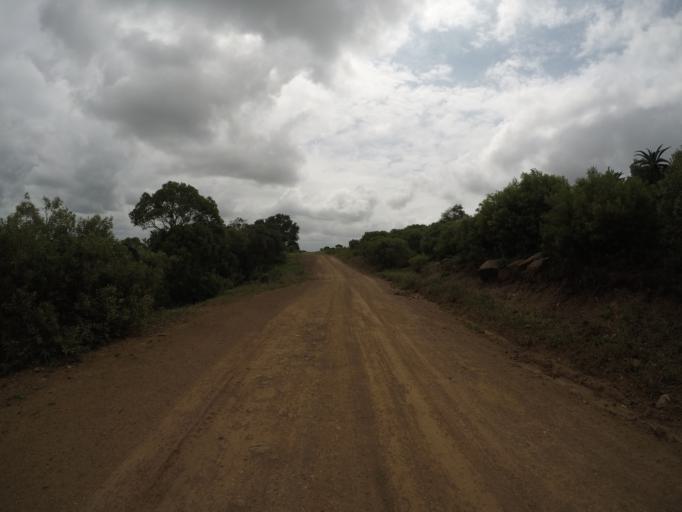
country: ZA
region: KwaZulu-Natal
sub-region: uThungulu District Municipality
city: Empangeni
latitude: -28.5799
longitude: 31.8672
